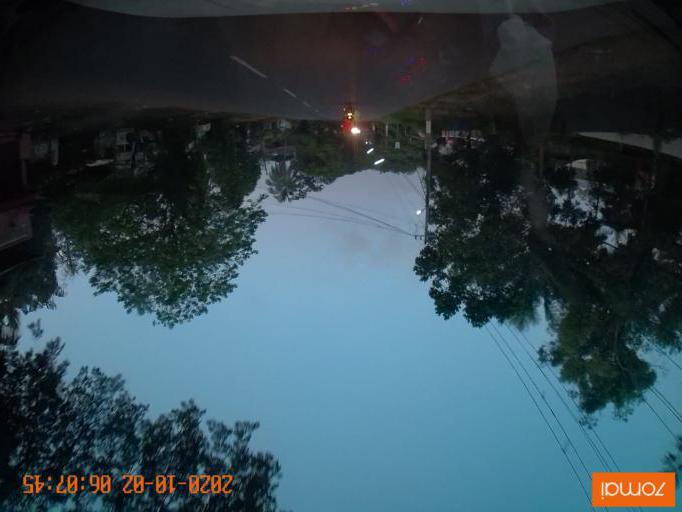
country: IN
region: Kerala
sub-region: Thrissur District
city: Avanoor
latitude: 10.6136
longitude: 76.1316
